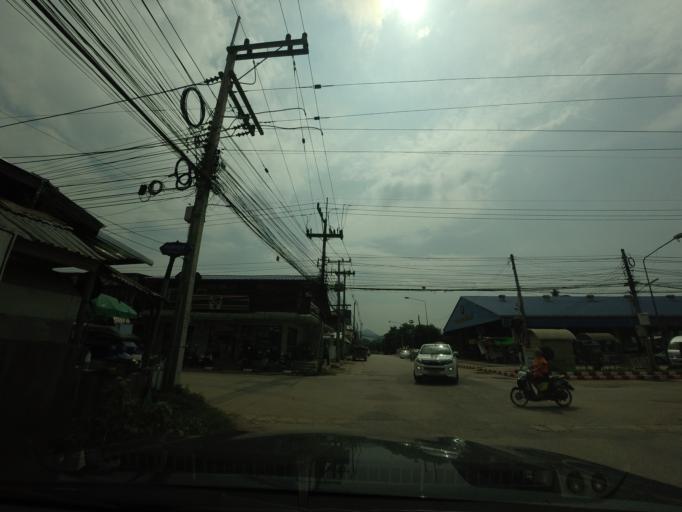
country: TH
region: Loei
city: Tha Li
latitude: 17.6251
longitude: 101.4223
